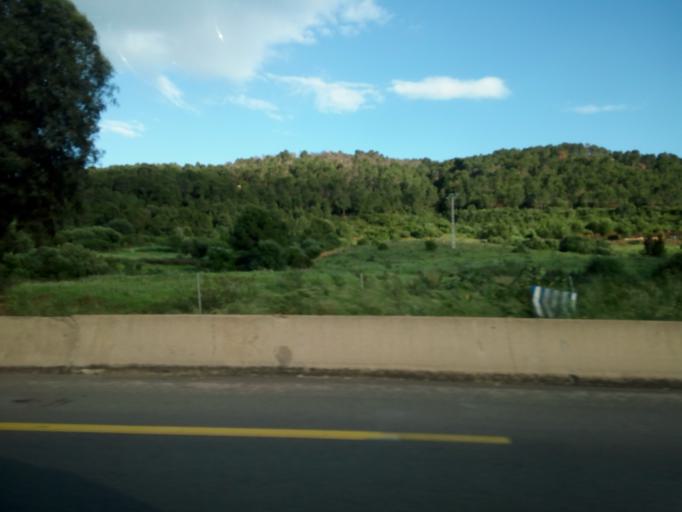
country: DZ
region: Tipaza
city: El Affroun
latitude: 36.4341
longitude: 2.5753
